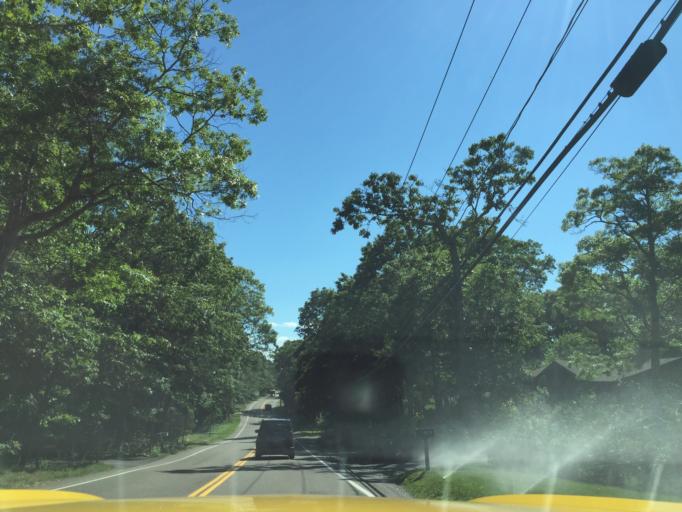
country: US
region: New York
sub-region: Suffolk County
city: North Sea
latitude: 40.9662
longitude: -72.3843
